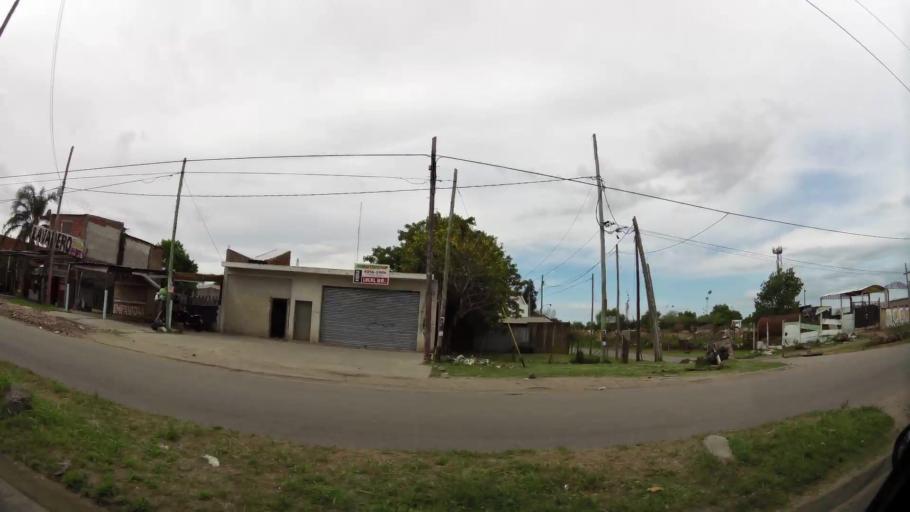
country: AR
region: Buenos Aires
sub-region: Partido de Quilmes
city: Quilmes
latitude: -34.7550
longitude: -58.2592
